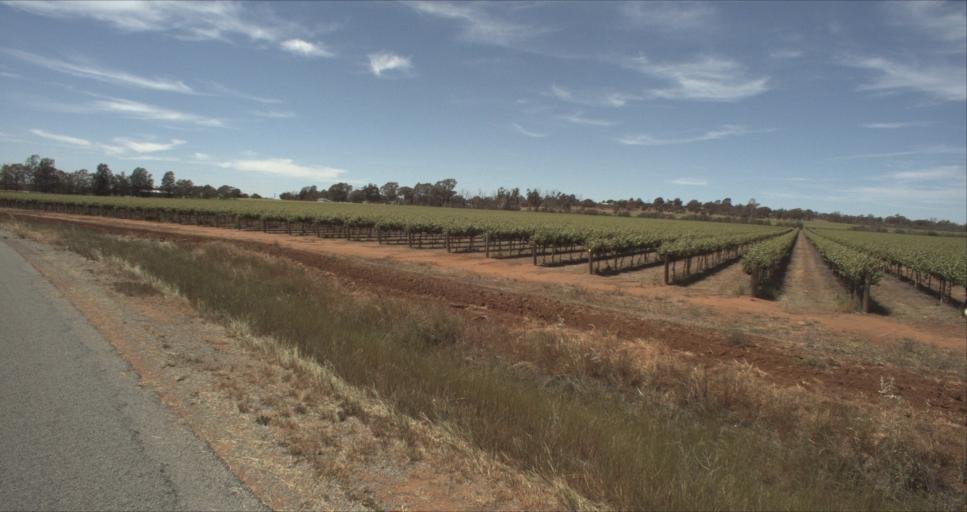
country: AU
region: New South Wales
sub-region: Leeton
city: Leeton
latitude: -34.5701
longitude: 146.4404
